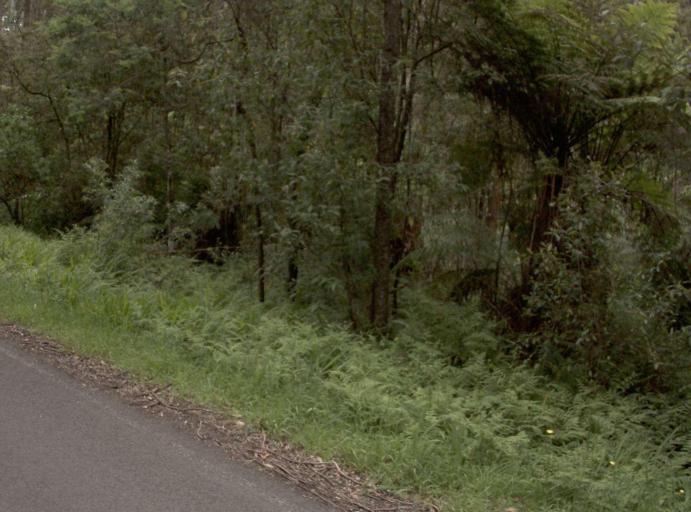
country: AU
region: Victoria
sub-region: Baw Baw
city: Warragul
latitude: -37.9234
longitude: 146.1093
